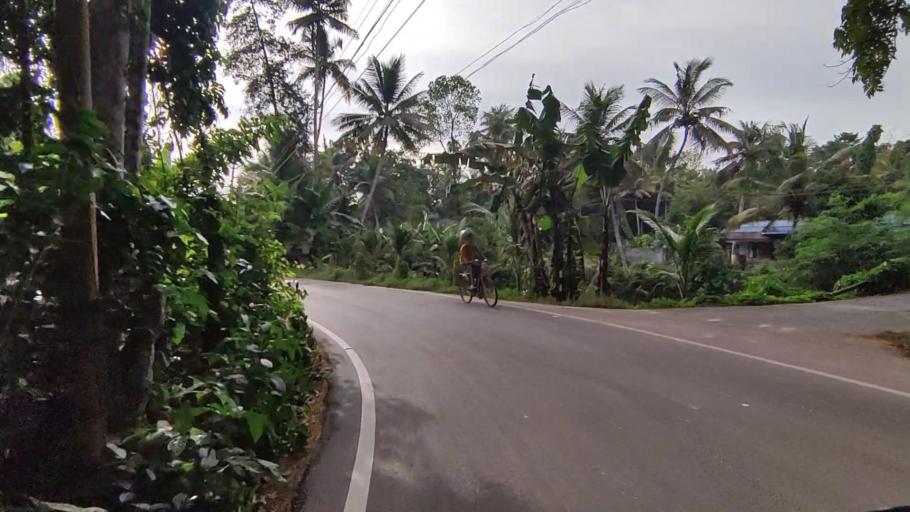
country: IN
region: Kerala
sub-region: Kottayam
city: Kottayam
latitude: 9.6011
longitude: 76.4941
